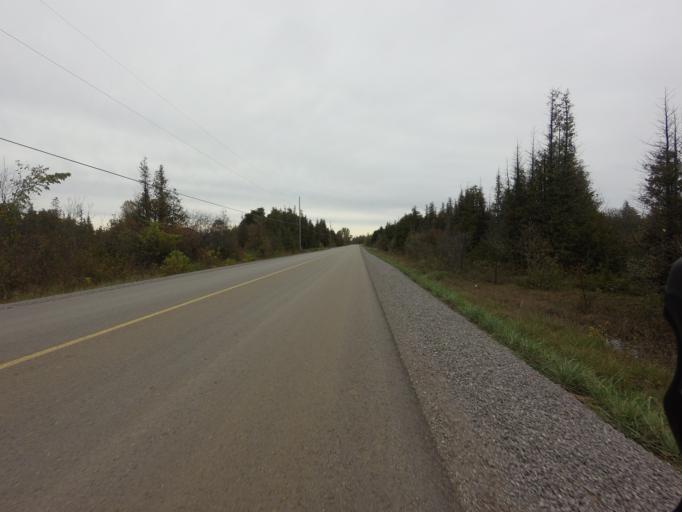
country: CA
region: Ontario
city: Brockville
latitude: 44.7760
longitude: -75.7560
